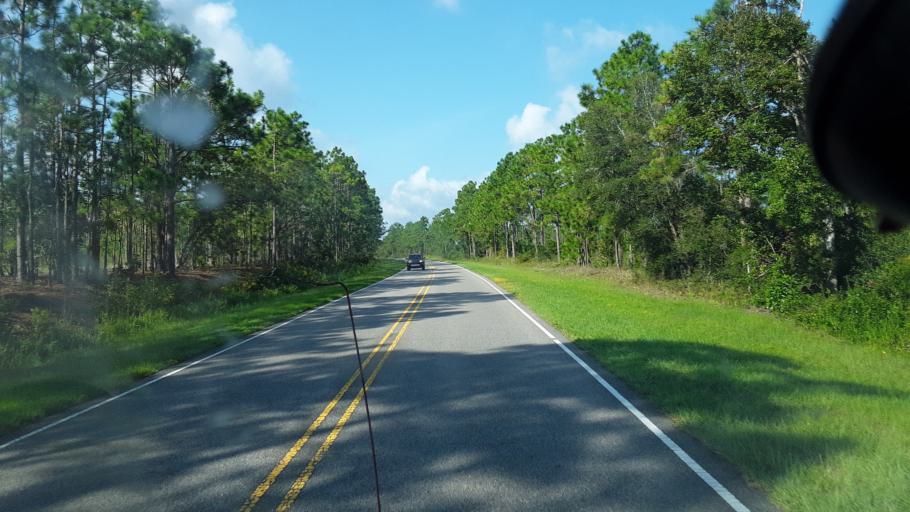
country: US
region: North Carolina
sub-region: Brunswick County
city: Boiling Spring Lakes
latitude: 34.0507
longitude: -77.9947
